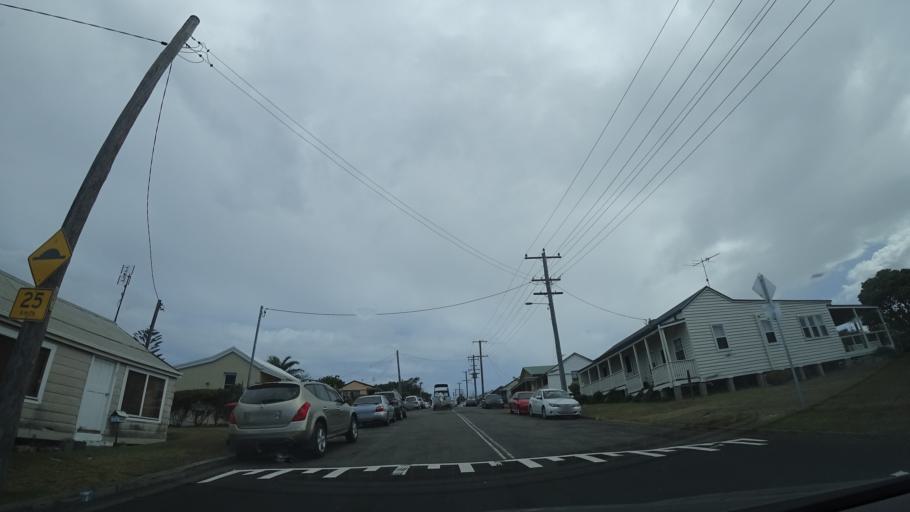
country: AU
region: New South Wales
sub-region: Wyong Shire
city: Kingfisher Shores
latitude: -33.1584
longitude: 151.6272
